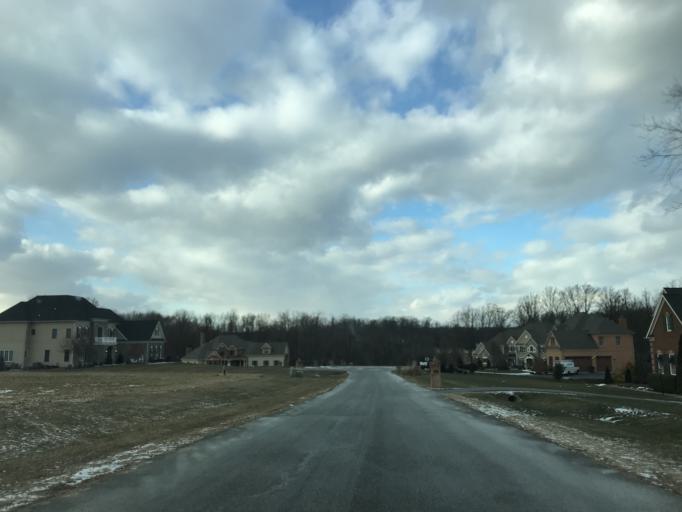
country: US
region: Maryland
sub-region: Harford County
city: Bel Air North
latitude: 39.6108
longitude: -76.3854
